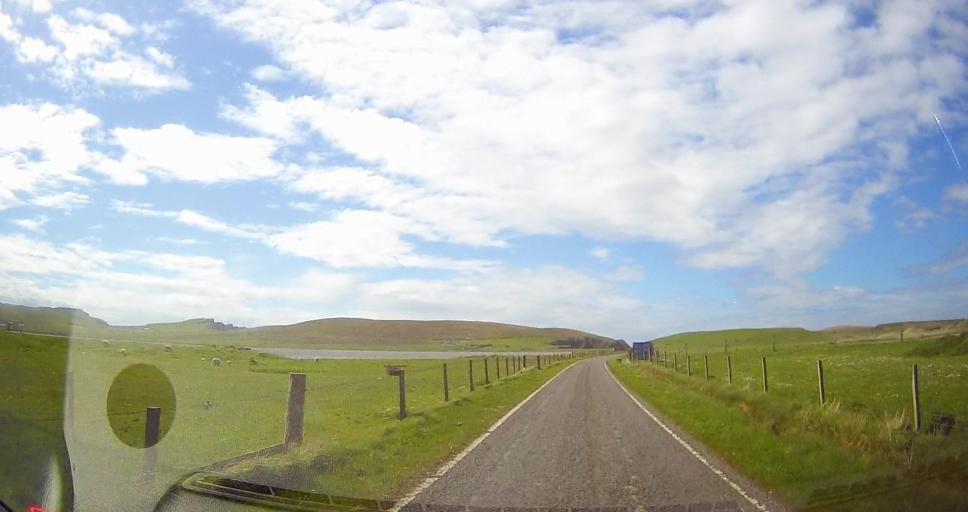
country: GB
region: Scotland
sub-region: Shetland Islands
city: Sandwick
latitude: 59.9414
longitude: -1.3302
